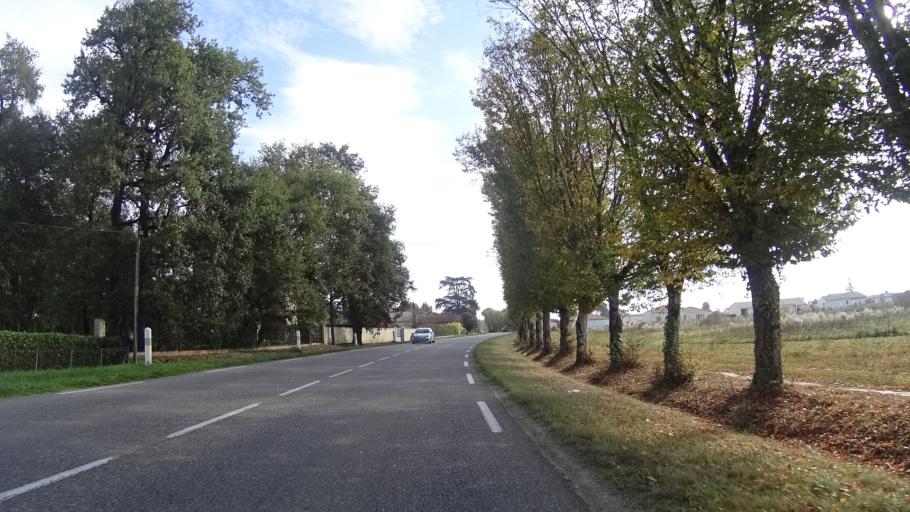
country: FR
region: Aquitaine
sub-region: Departement du Lot-et-Garonne
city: Brax
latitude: 44.2054
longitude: 0.5417
